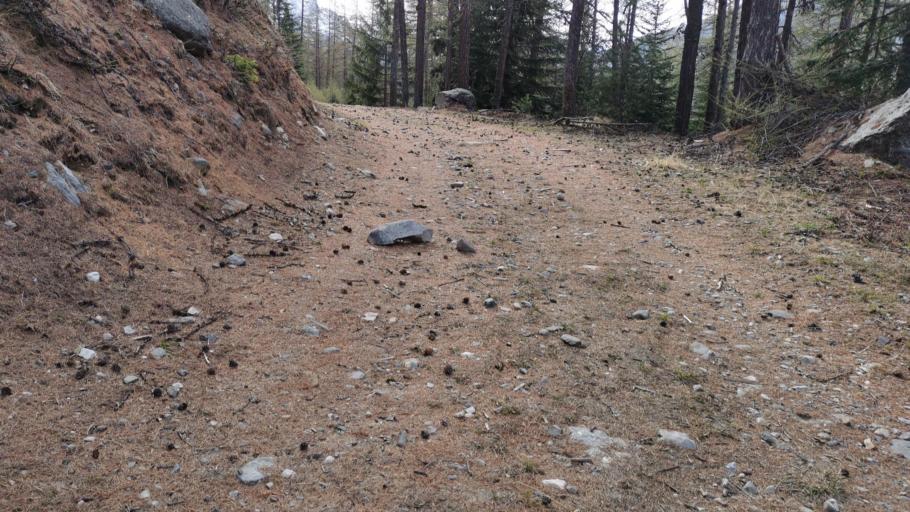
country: IT
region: Piedmont
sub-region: Provincia di Torino
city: Bardonecchia
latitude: 45.0148
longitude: 6.6336
